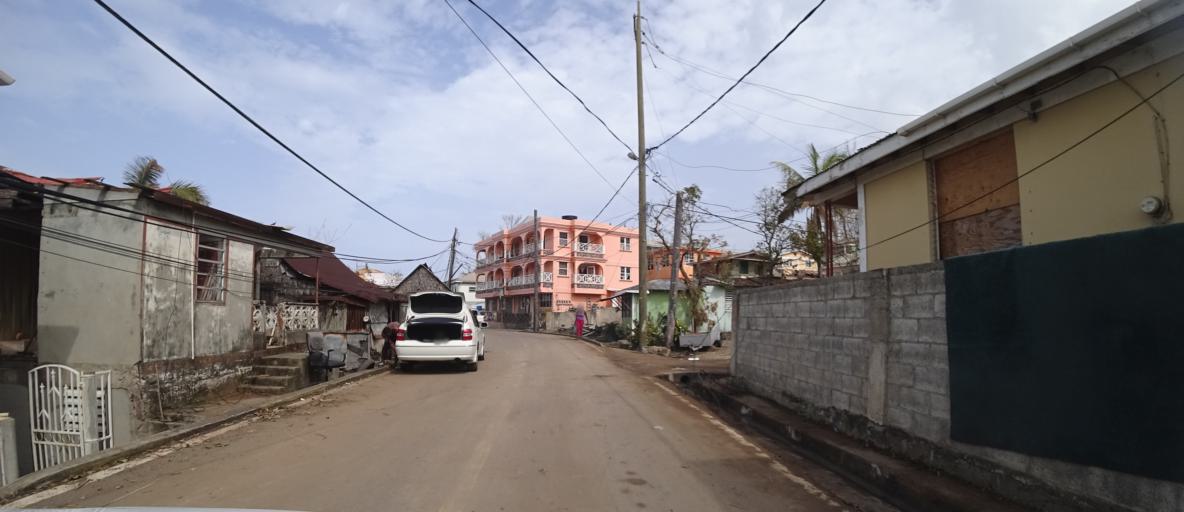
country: DM
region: Saint Paul
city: Mahaut
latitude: 15.3639
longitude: -61.3998
